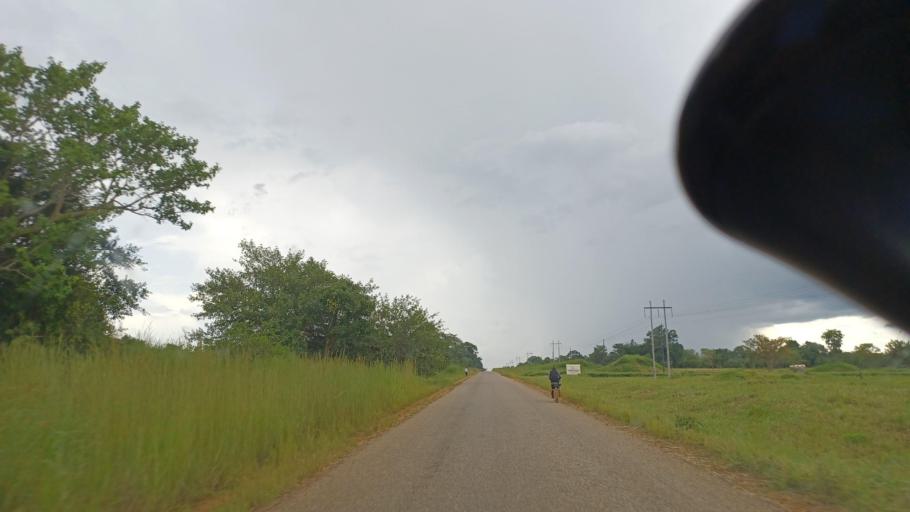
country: ZM
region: North-Western
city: Kasempa
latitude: -13.0207
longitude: 26.0005
